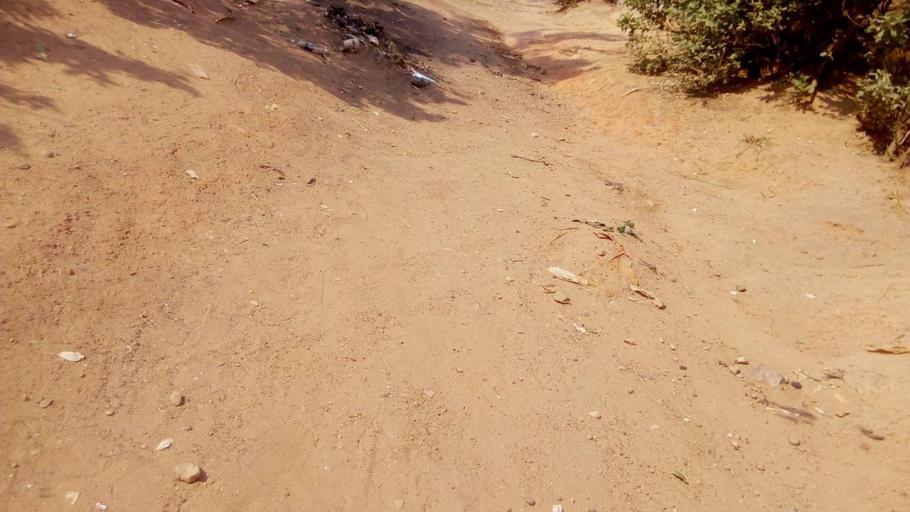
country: ZM
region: Lusaka
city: Lusaka
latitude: -15.3579
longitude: 28.2909
